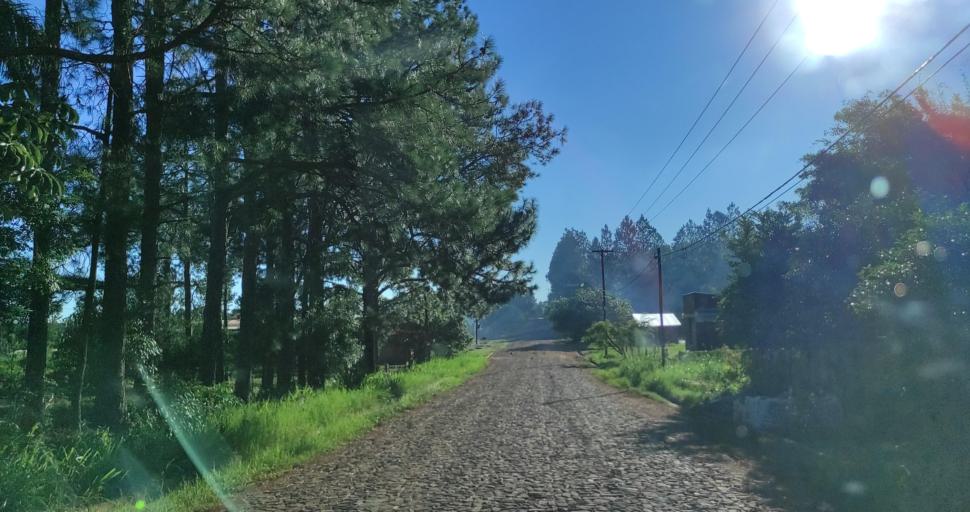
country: AR
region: Misiones
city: Puerto Rico
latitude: -26.8253
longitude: -55.0095
